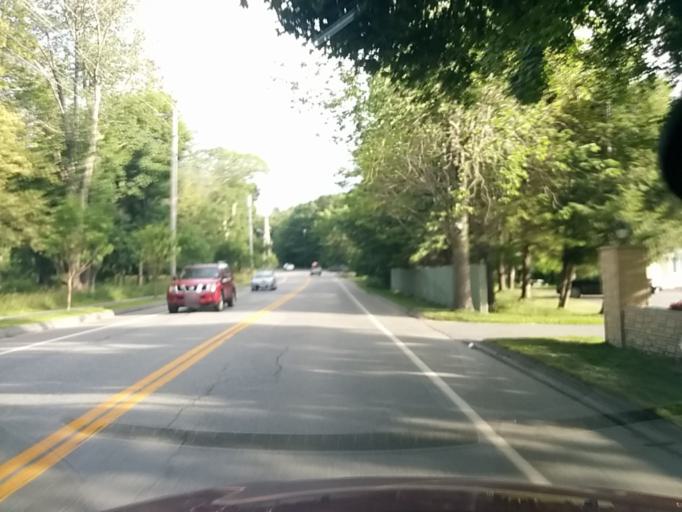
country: US
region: Maine
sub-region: Hancock County
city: Bar Harbor
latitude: 44.3809
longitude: -68.2024
